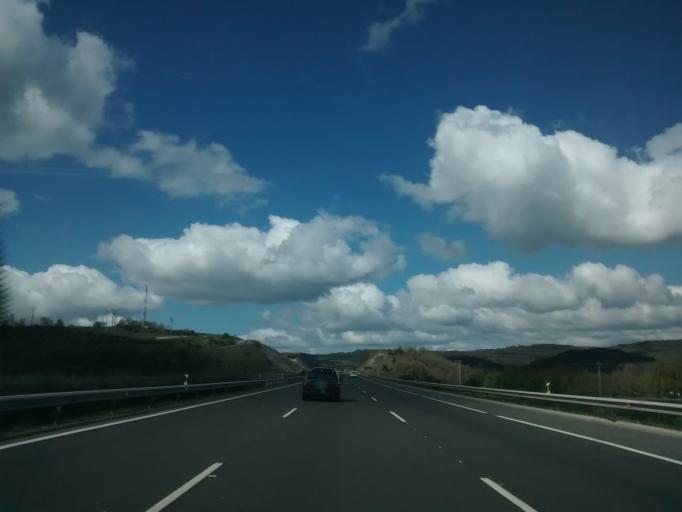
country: ES
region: Basque Country
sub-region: Provincia de Alava
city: Arminon
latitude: 42.7486
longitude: -2.8448
